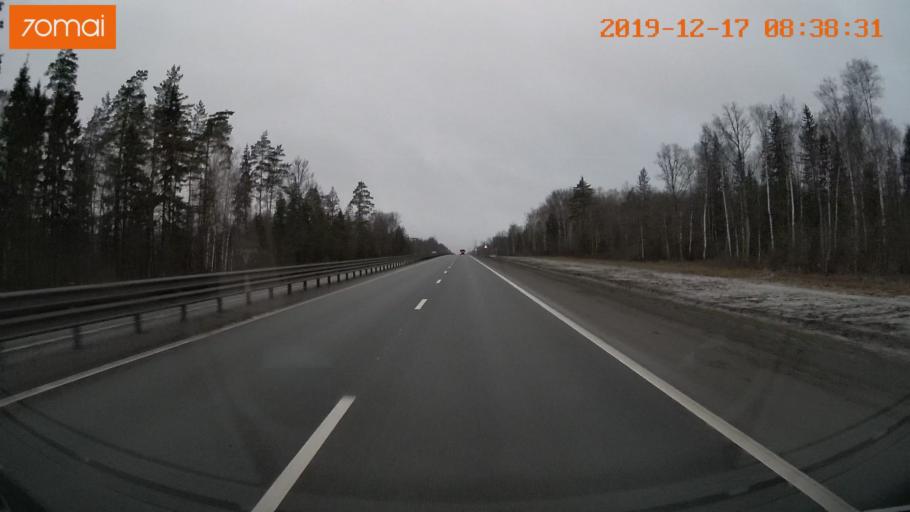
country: RU
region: Vladimir
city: Lakinsk
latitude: 55.9799
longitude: 39.8315
